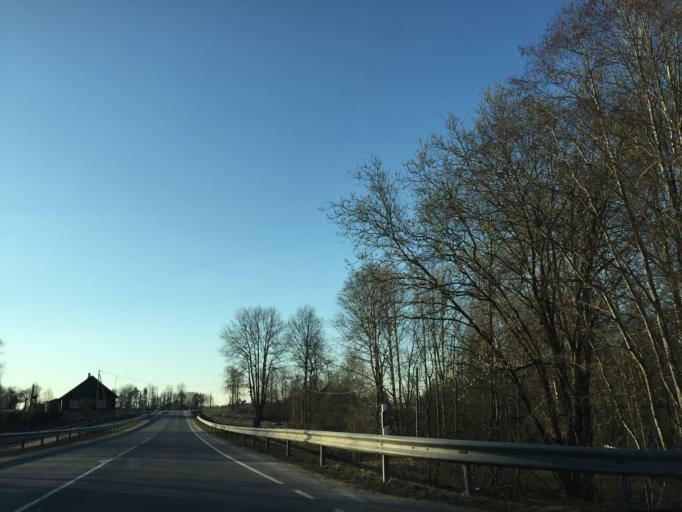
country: EE
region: Ida-Virumaa
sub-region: Johvi vald
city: Johvi
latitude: 59.2210
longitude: 27.5129
